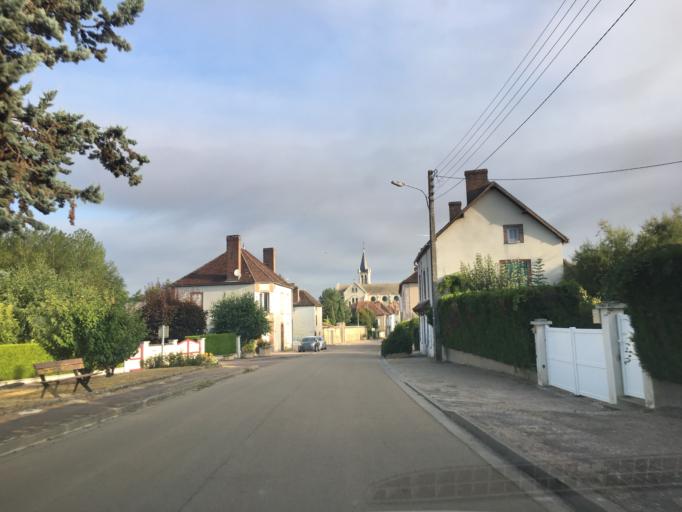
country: FR
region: Bourgogne
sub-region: Departement de l'Yonne
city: Aillant-sur-Tholon
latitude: 47.8718
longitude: 3.3518
